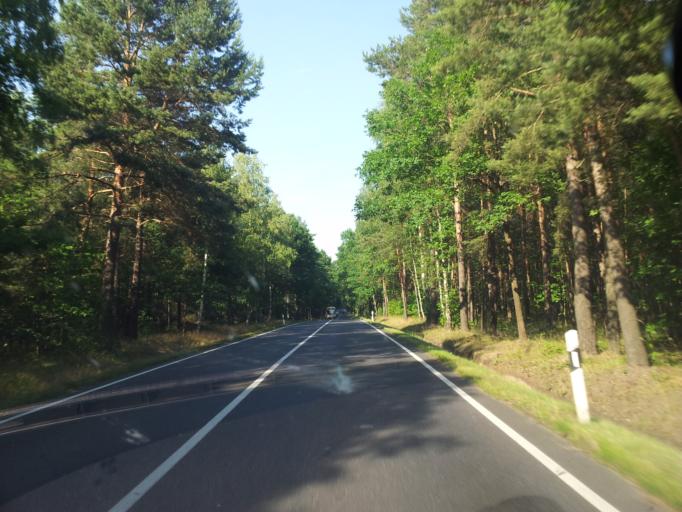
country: DE
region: Saxony
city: Schwepnitz
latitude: 51.3124
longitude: 13.9268
